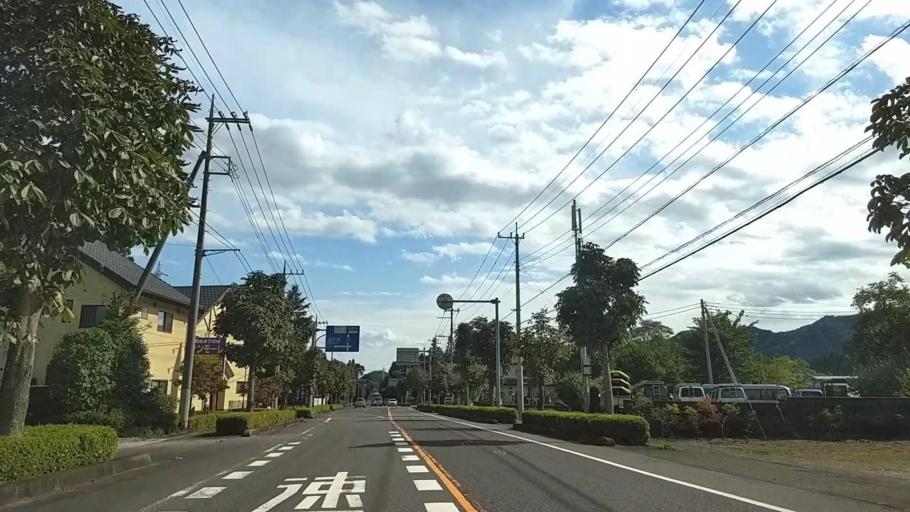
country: JP
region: Tochigi
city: Imaichi
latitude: 36.7958
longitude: 139.7010
